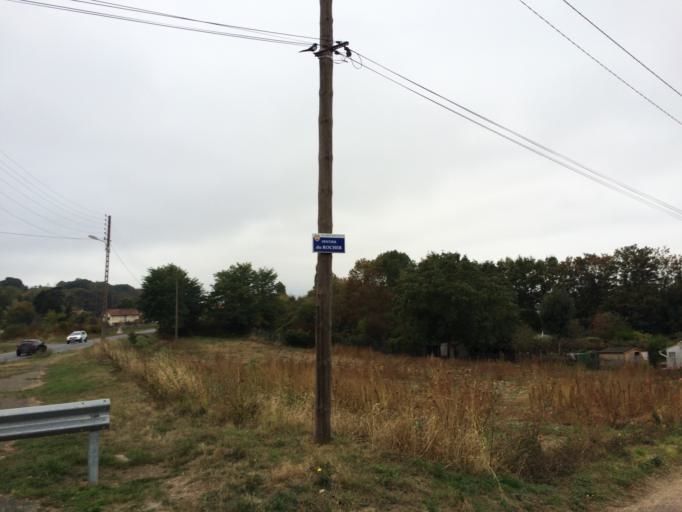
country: FR
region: Ile-de-France
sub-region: Departement de l'Essonne
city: Villebon-sur-Yvette
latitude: 48.6970
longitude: 2.2441
